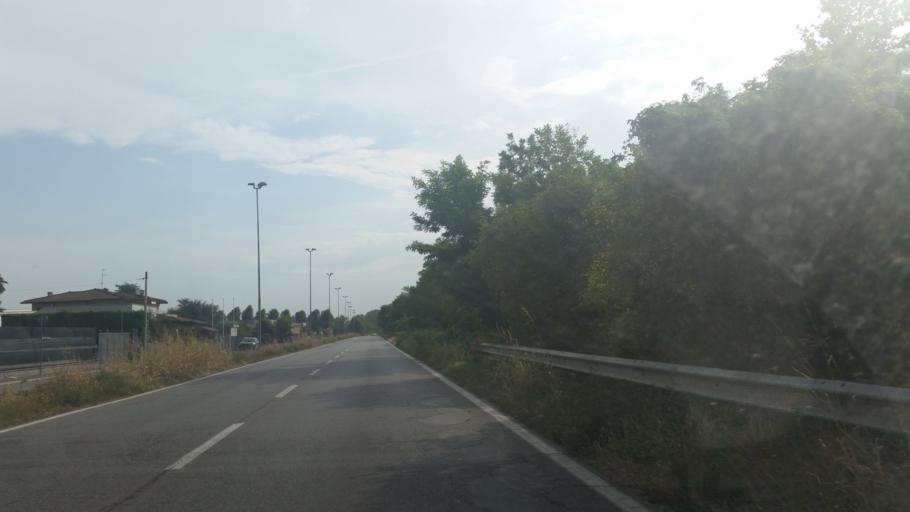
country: IT
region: Lombardy
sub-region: Provincia di Brescia
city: Barbariga
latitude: 45.3969
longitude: 10.0691
